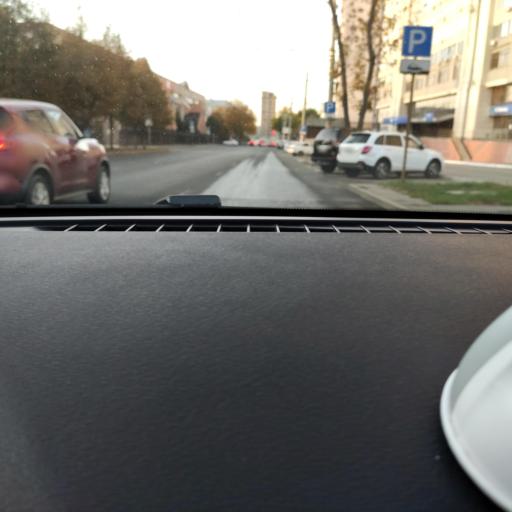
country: RU
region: Samara
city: Samara
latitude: 53.1910
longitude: 50.1209
